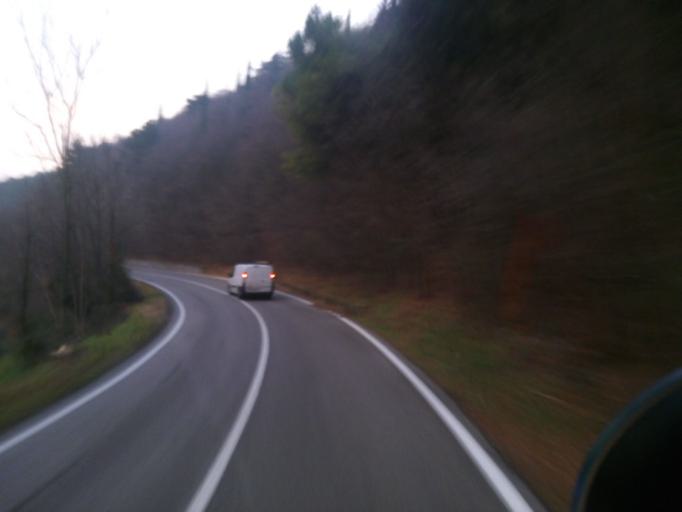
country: IT
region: Veneto
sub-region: Provincia di Verona
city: Fumane
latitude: 45.5585
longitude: 10.8656
